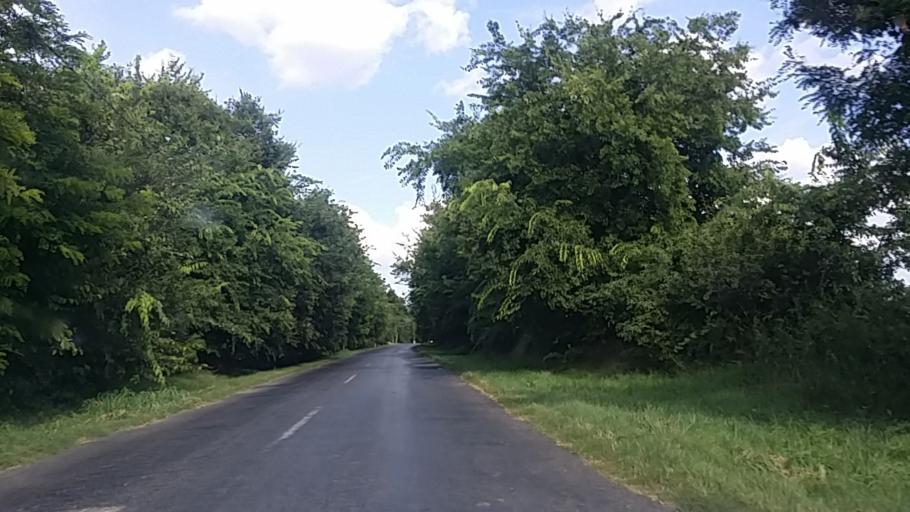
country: HU
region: Tolna
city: Szedres
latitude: 46.5158
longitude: 18.6145
